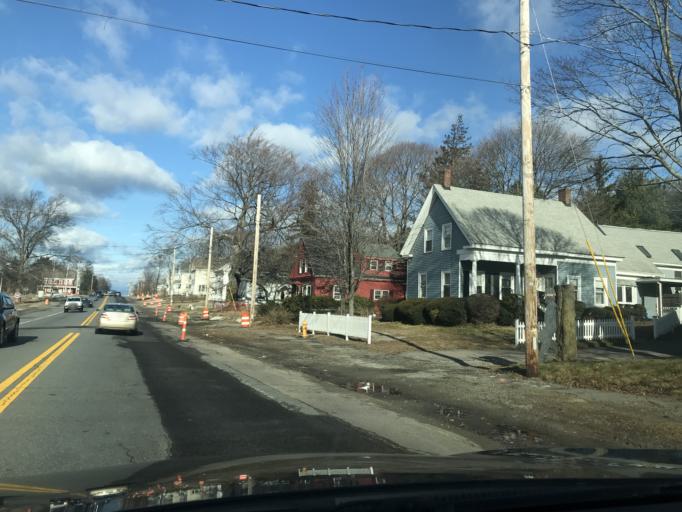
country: US
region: Massachusetts
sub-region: Norfolk County
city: Weymouth
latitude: 42.1834
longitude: -70.9553
